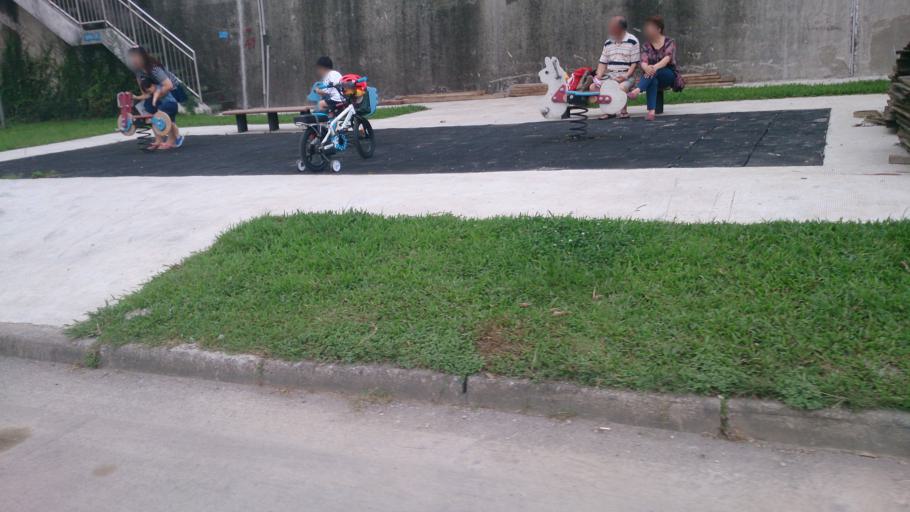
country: TW
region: Taipei
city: Taipei
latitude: 25.0600
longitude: 121.5981
